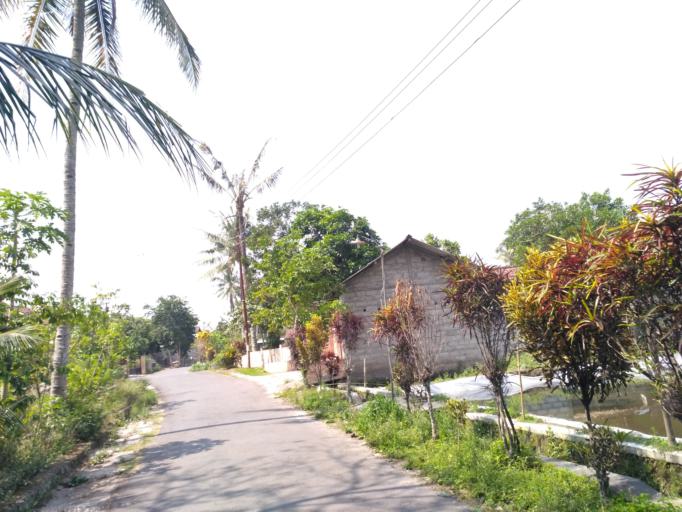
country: ID
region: Daerah Istimewa Yogyakarta
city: Depok
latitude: -7.7107
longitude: 110.4195
